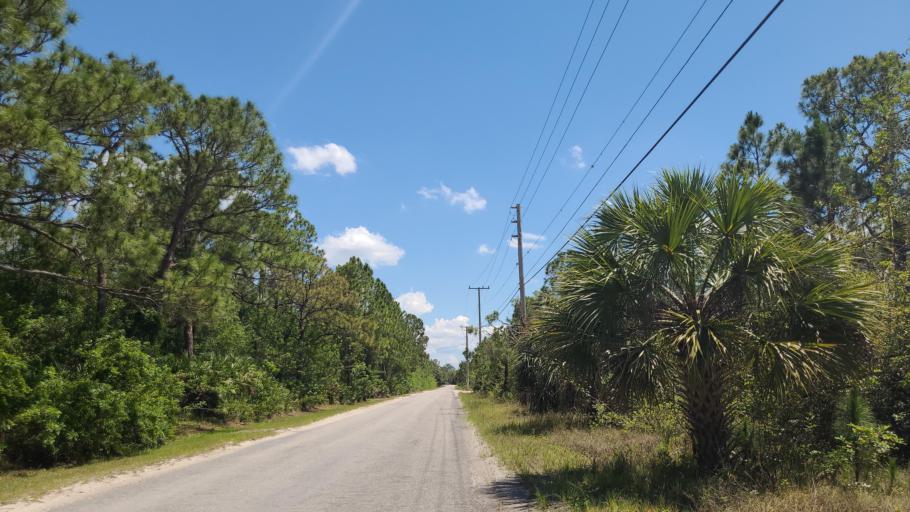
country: US
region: Florida
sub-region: Indian River County
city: Fellsmere
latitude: 27.7405
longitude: -80.5935
